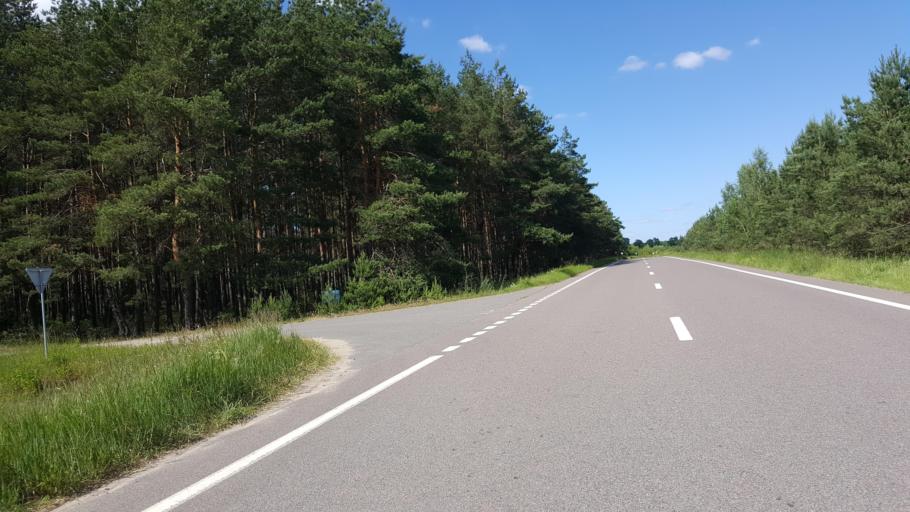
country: PL
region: Podlasie
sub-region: Powiat hajnowski
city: Hajnowka
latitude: 52.5602
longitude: 23.6049
